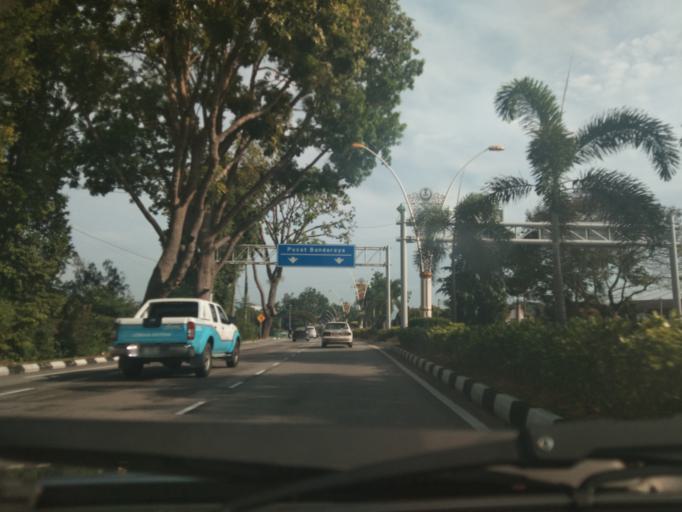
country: MY
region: Perak
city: Ipoh
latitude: 4.5833
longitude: 101.1016
